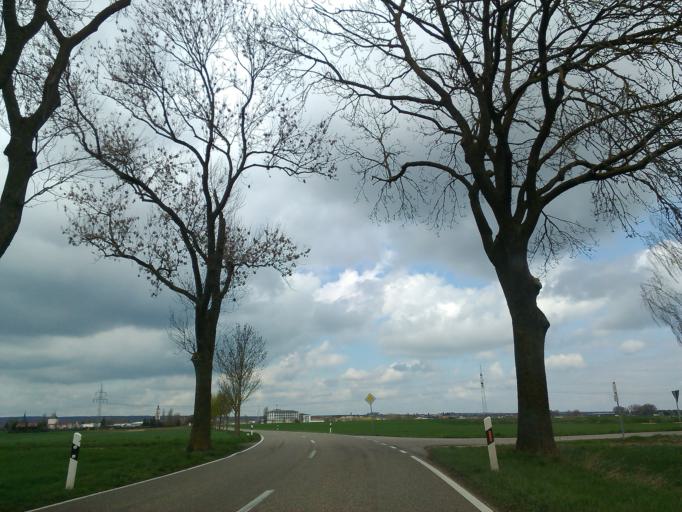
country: DE
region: Baden-Wuerttemberg
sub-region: Tuebingen Region
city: Langenau
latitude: 48.4874
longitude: 10.1386
